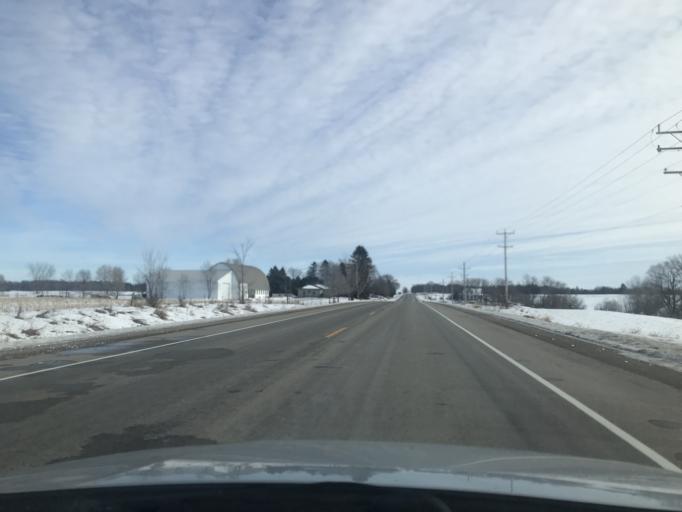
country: US
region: Wisconsin
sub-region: Oconto County
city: Oconto Falls
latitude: 44.8947
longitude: -88.1840
